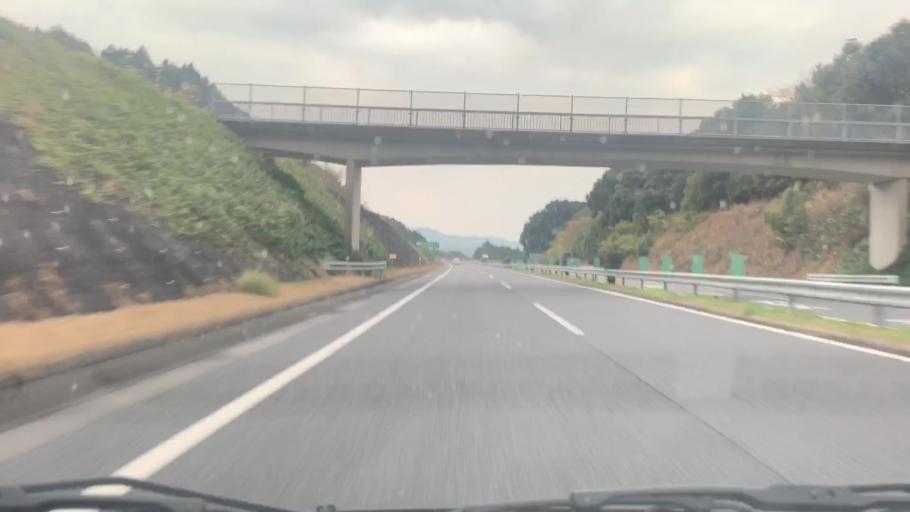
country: JP
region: Nagasaki
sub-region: Isahaya-shi
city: Isahaya
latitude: 32.8221
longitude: 129.9934
